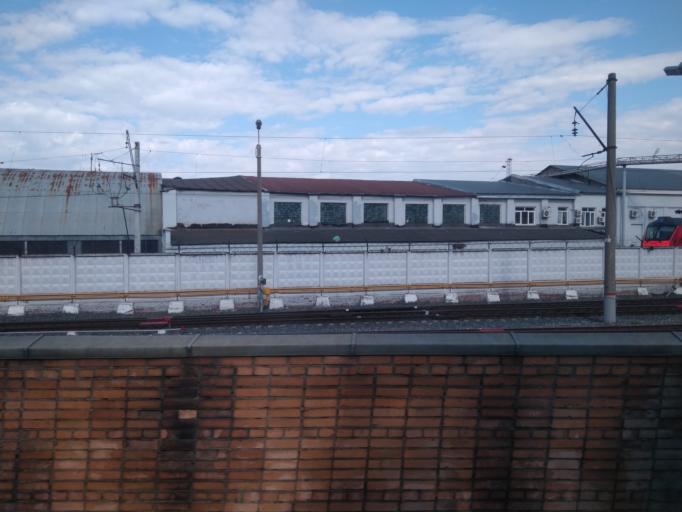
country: RU
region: Moscow
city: Mar'ina Roshcha
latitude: 55.7875
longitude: 37.6424
